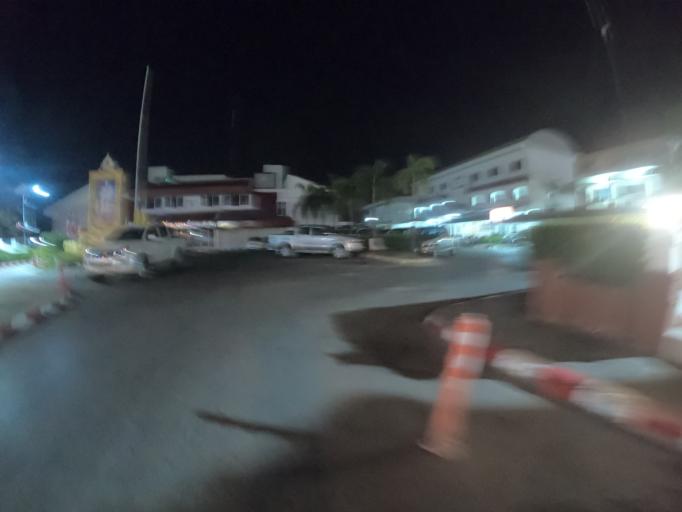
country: TH
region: Khon Kaen
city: Khon Kaen
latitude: 16.4286
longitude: 102.8356
